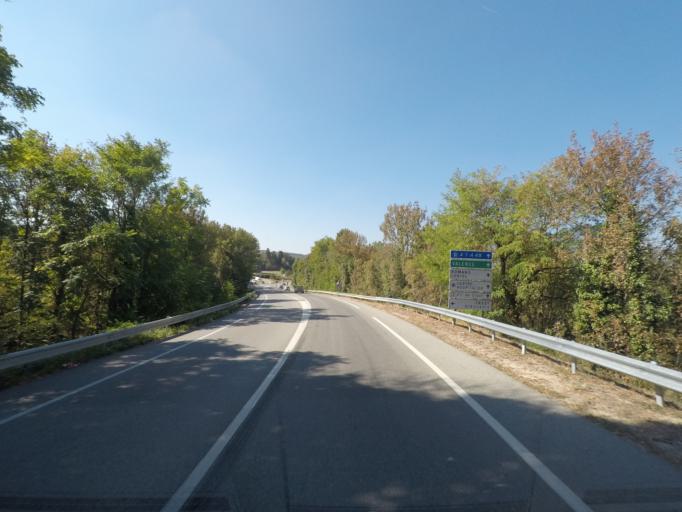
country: FR
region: Rhone-Alpes
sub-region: Departement de la Drome
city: Crest
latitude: 44.7229
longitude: 5.0182
